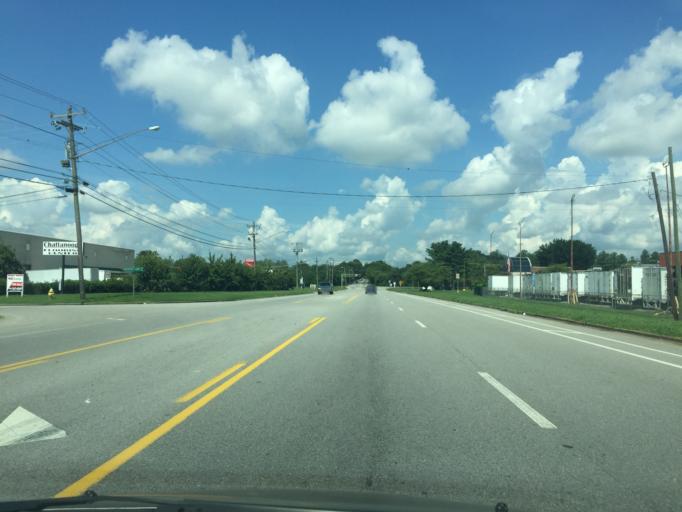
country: US
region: Tennessee
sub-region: Hamilton County
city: East Chattanooga
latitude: 35.0549
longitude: -85.1966
